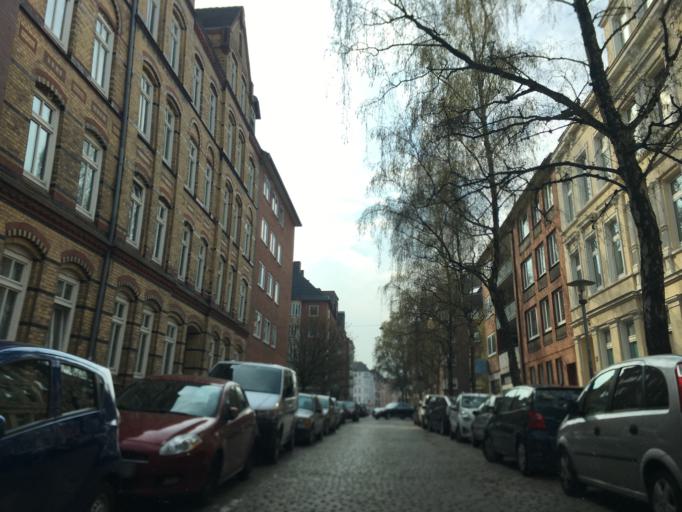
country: DE
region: Schleswig-Holstein
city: Kiel
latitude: 54.3382
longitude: 10.1365
